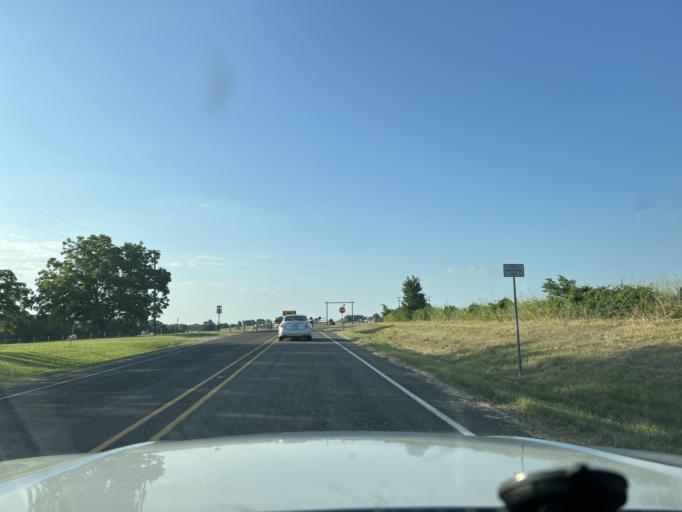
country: US
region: Texas
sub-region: Washington County
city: Brenham
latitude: 30.2288
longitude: -96.3917
